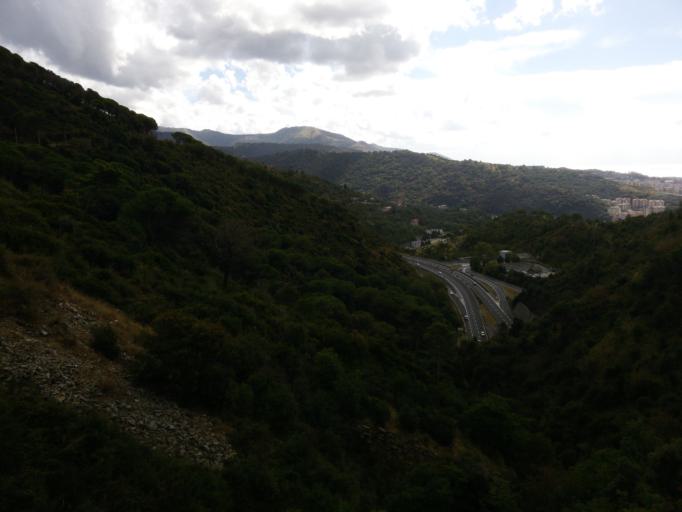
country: IT
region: Liguria
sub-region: Provincia di Genova
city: Genoa
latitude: 44.4398
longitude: 8.9369
